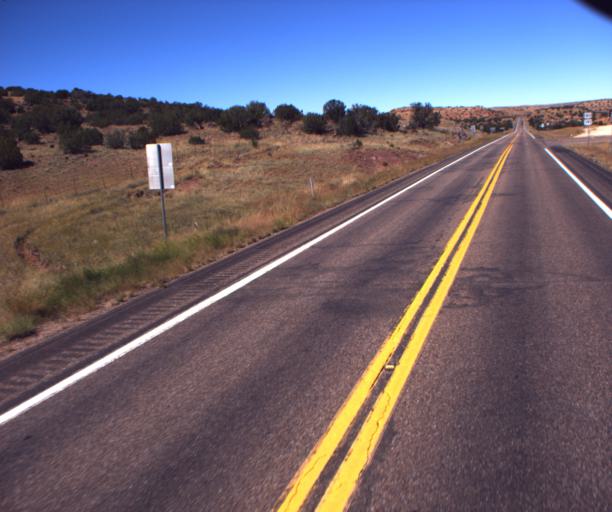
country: US
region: Arizona
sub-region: Apache County
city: Saint Johns
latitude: 34.3624
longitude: -109.3855
